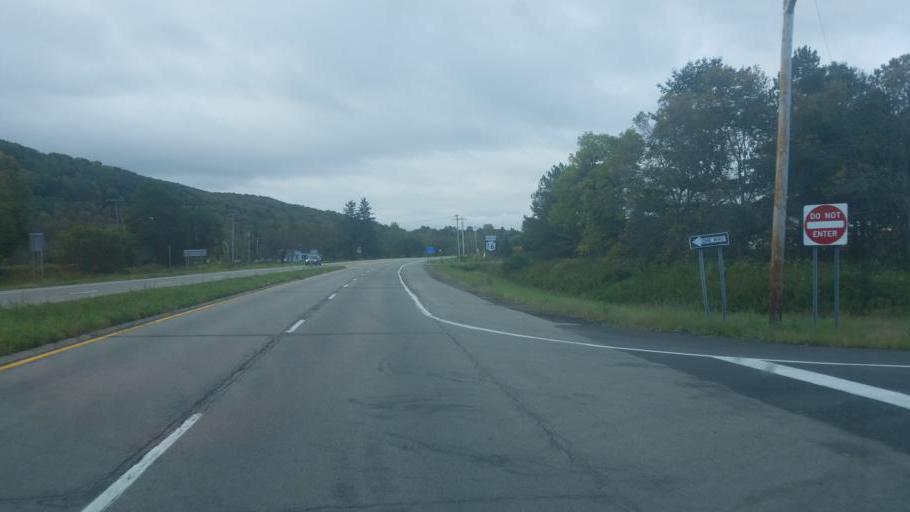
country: US
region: New York
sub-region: Cattaraugus County
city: Weston Mills
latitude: 42.1746
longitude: -78.3832
